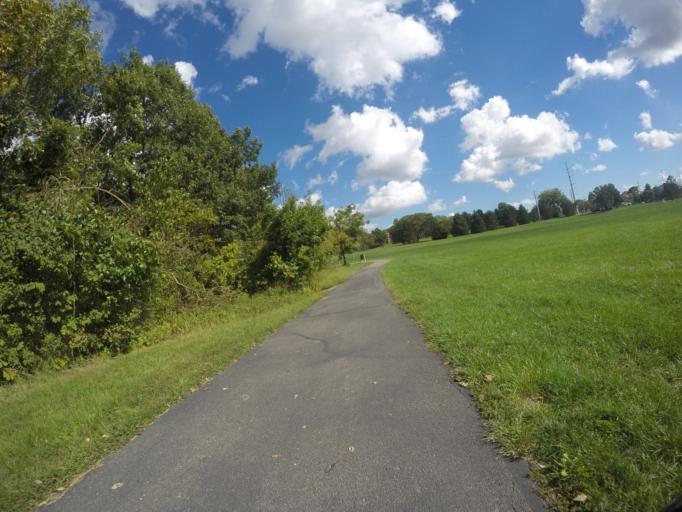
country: US
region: Kansas
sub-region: Johnson County
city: Lenexa
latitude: 38.9201
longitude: -94.7015
